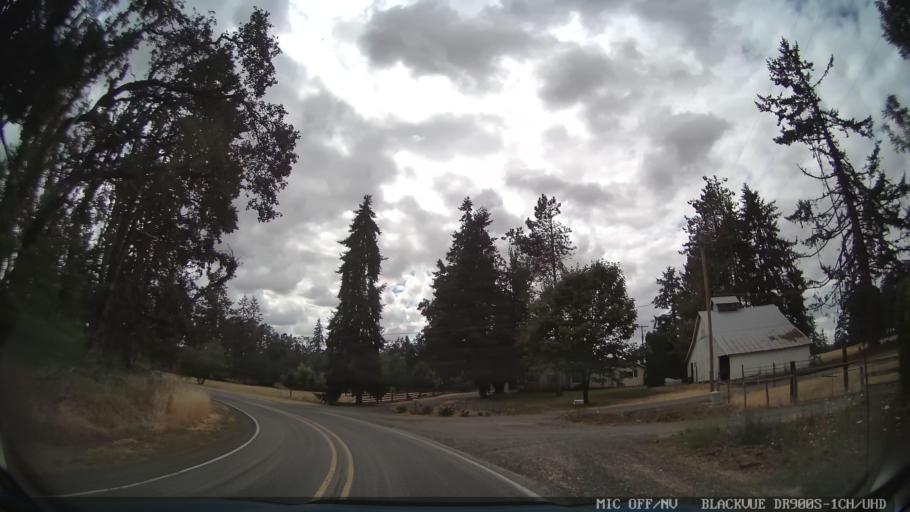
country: US
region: Oregon
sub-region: Marion County
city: Sublimity
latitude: 44.8442
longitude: -122.7736
